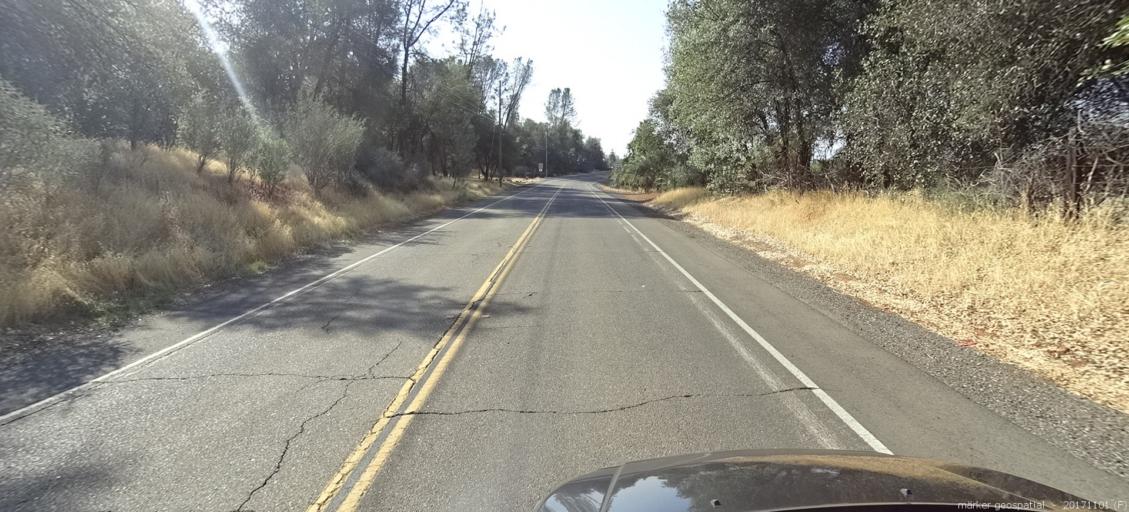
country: US
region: California
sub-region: Shasta County
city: Shasta Lake
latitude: 40.6847
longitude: -122.3449
